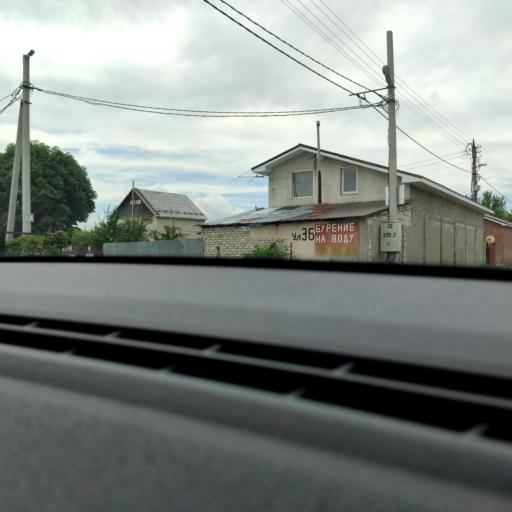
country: RU
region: Samara
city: Podstepki
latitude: 53.5073
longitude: 49.1632
